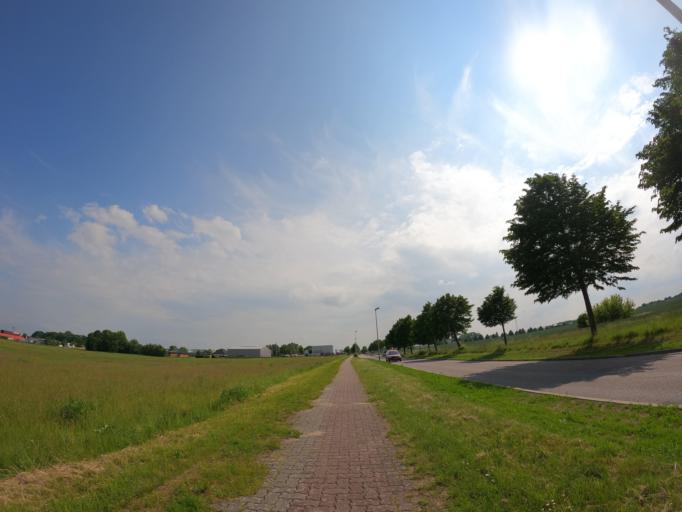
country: DE
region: Mecklenburg-Vorpommern
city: Stralsund
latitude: 54.2848
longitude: 13.0588
